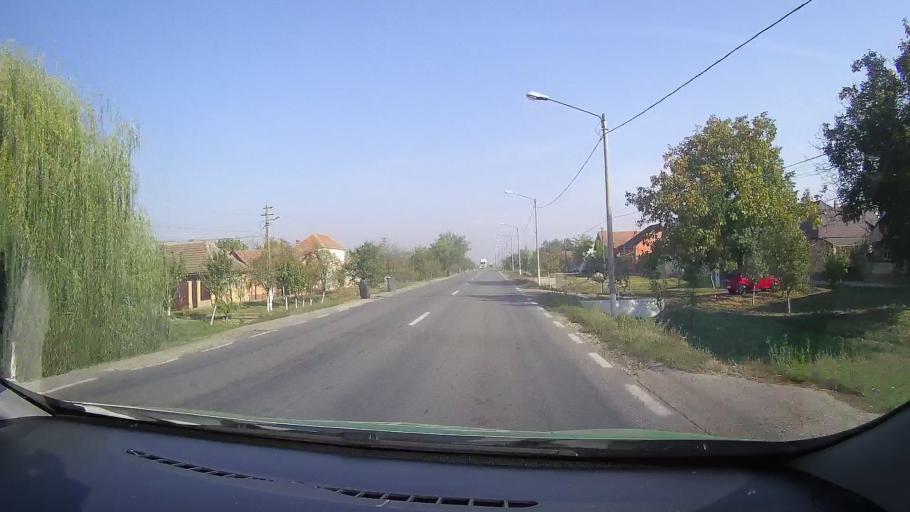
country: RO
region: Arad
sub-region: Comuna Pilu
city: Pilu
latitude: 46.5796
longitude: 21.3433
